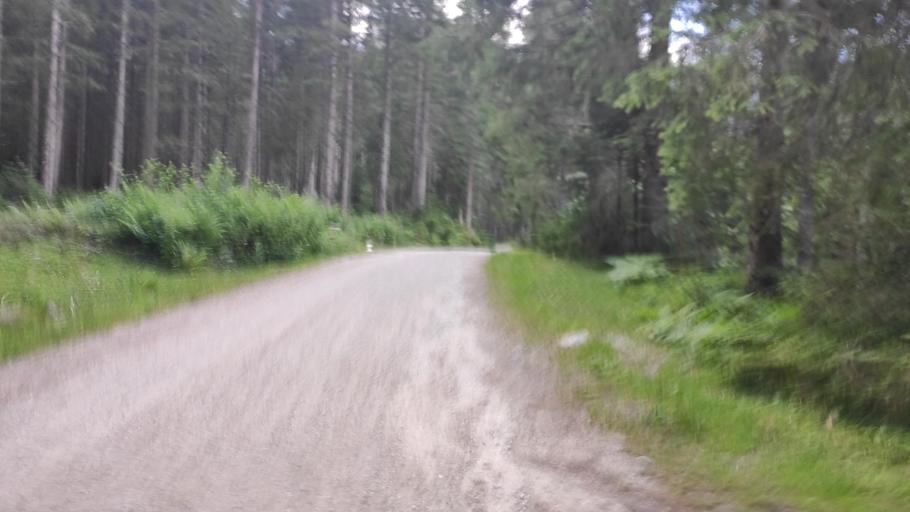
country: AT
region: Salzburg
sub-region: Politischer Bezirk Zell am See
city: Krimml
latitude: 47.2216
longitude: 12.1852
